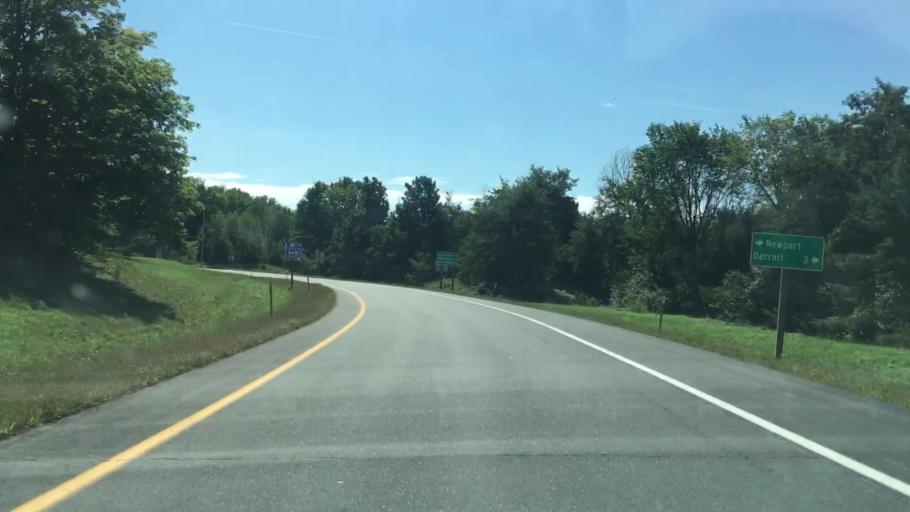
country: US
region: Maine
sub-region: Penobscot County
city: Newport
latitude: 44.8333
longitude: -69.2950
